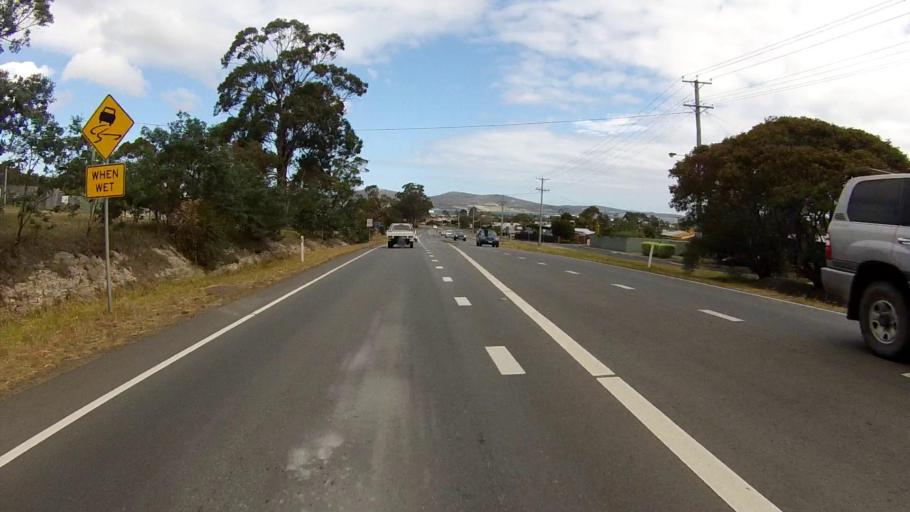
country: AU
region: Tasmania
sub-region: Clarence
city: Rokeby
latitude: -42.8935
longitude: 147.4366
